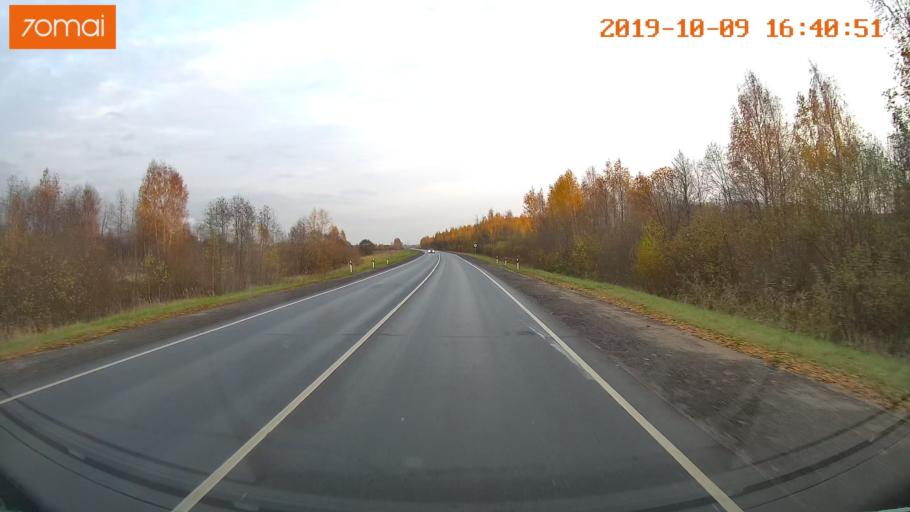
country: RU
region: Kostroma
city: Volgorechensk
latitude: 57.4788
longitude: 41.0683
